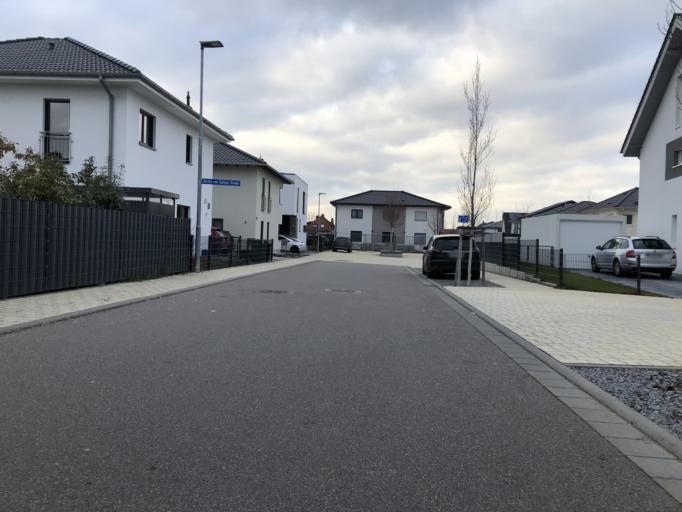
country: DE
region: Baden-Wuerttemberg
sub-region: Karlsruhe Region
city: Altlussheim
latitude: 49.3000
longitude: 8.5067
